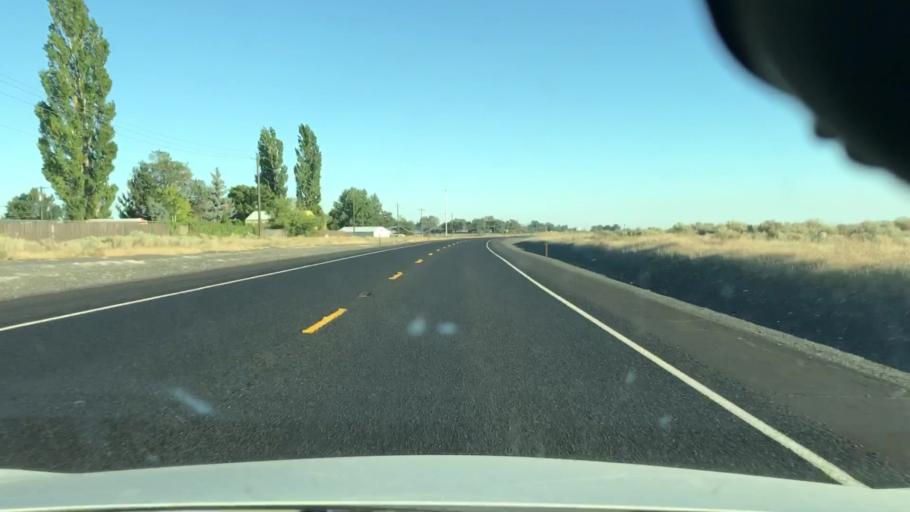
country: US
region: Washington
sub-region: Grant County
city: Moses Lake North
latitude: 47.1774
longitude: -119.3325
